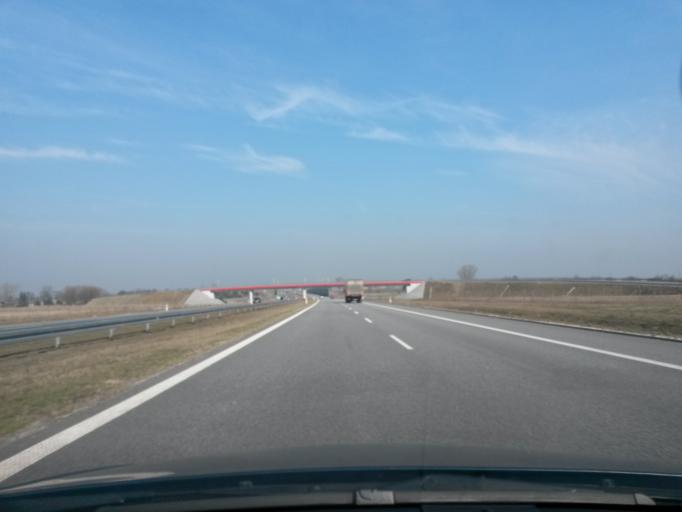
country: PL
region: Lodz Voivodeship
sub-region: Powiat kutnowski
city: Krzyzanow
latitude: 52.1976
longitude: 19.4867
